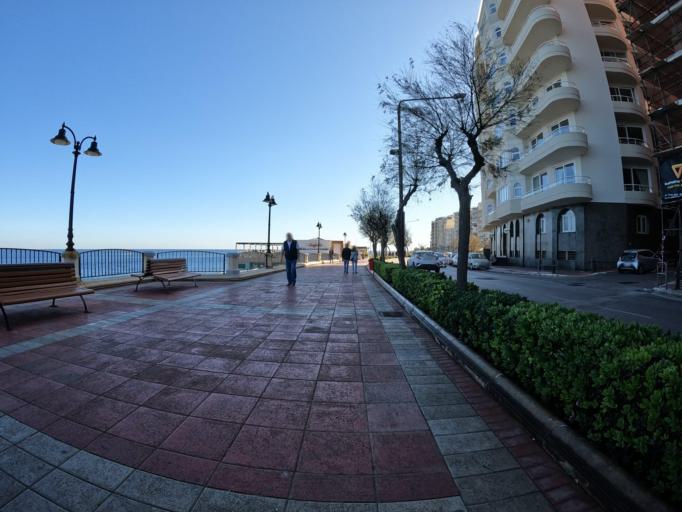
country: MT
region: Tas-Sliema
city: Sliema
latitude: 35.9164
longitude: 14.5033
